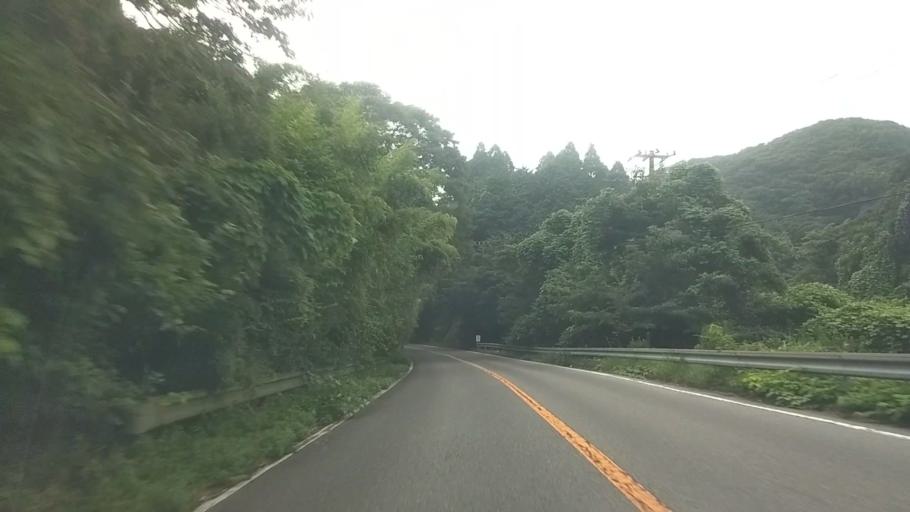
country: JP
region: Chiba
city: Katsuura
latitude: 35.1663
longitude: 140.3225
